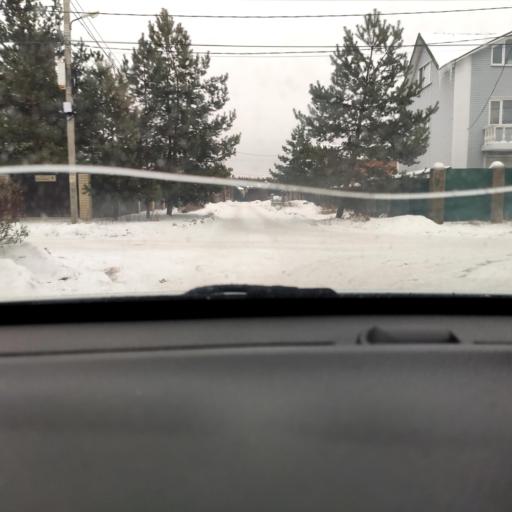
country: RU
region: Voronezj
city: Somovo
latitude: 51.7113
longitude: 39.3177
